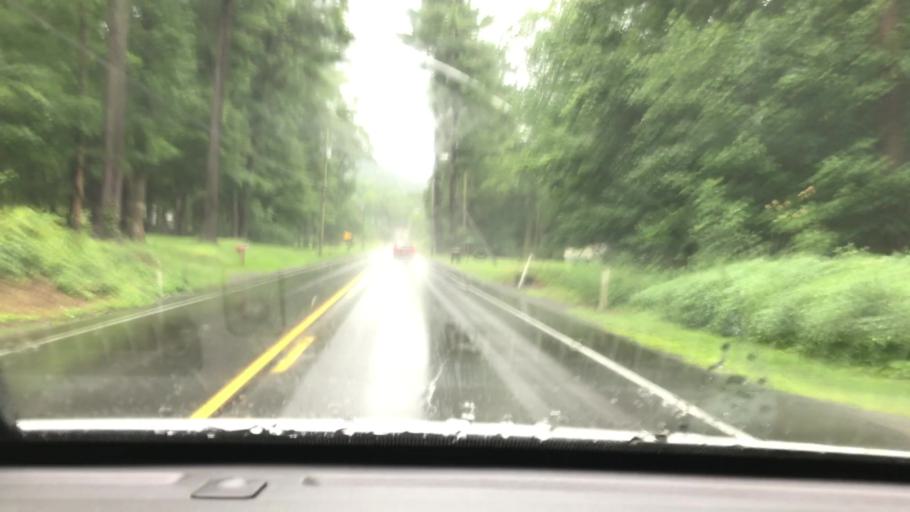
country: US
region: Pennsylvania
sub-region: Blair County
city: Tyrone
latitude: 40.7498
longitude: -78.2146
